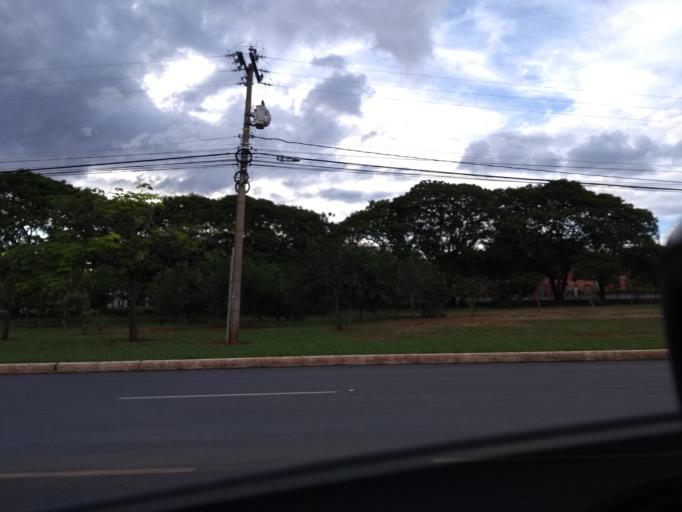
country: BR
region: Federal District
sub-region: Brasilia
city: Brasilia
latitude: -15.7950
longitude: -47.9099
